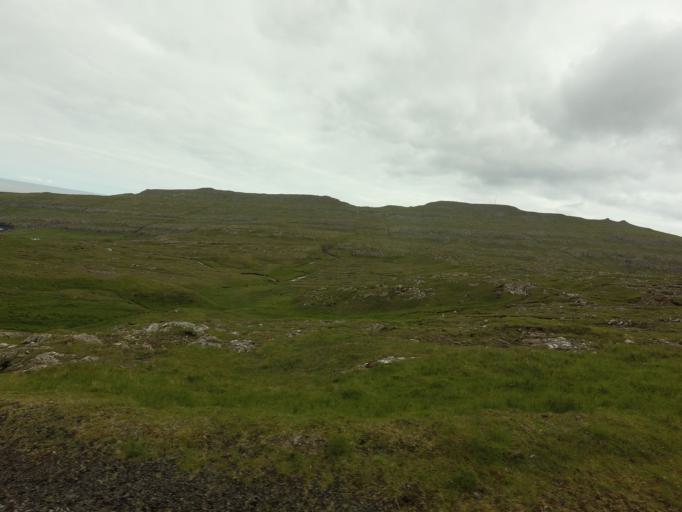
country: FO
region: Suduroy
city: Vagur
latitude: 61.4405
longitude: -6.7468
